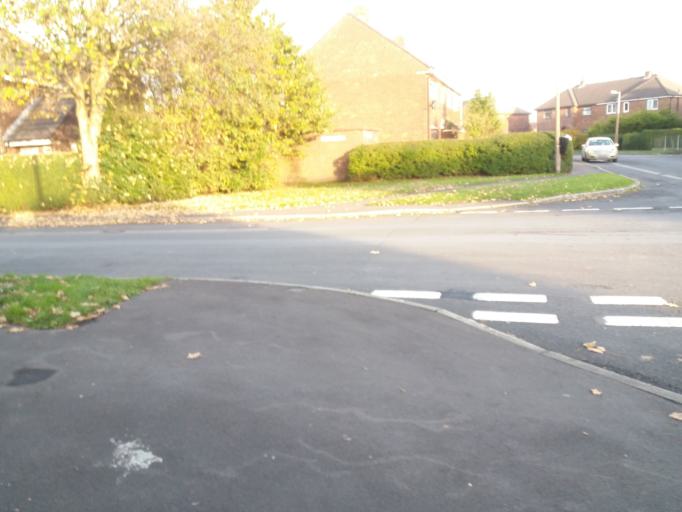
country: GB
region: England
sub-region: Lancashire
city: Coppull
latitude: 53.6243
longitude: -2.6637
